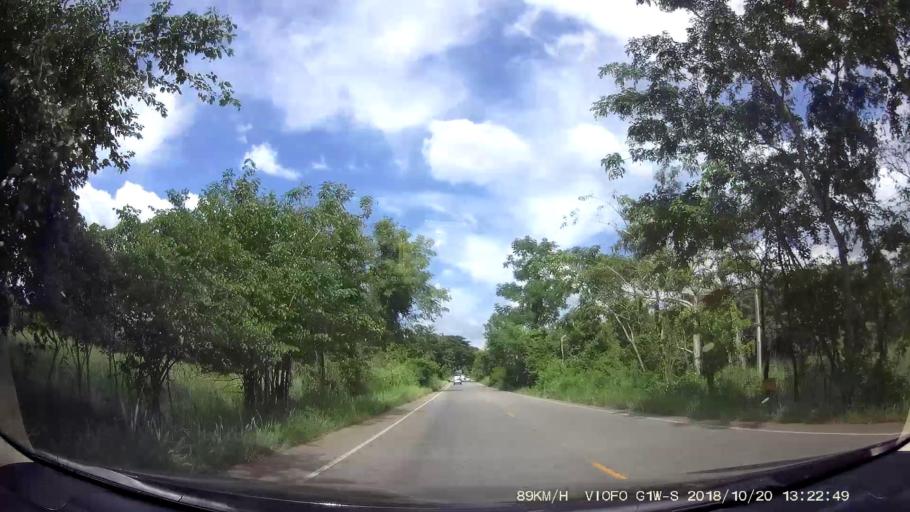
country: TH
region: Chaiyaphum
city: Khon San
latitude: 16.5762
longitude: 101.9179
